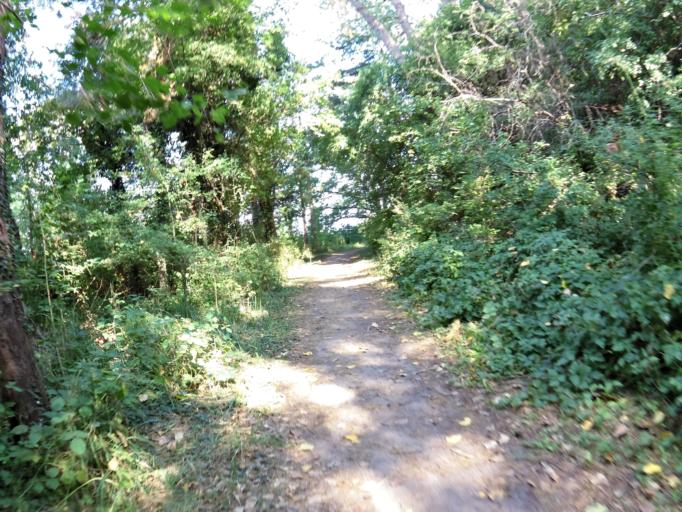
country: DE
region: Mecklenburg-Vorpommern
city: Loddin
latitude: 53.9661
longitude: 14.0435
